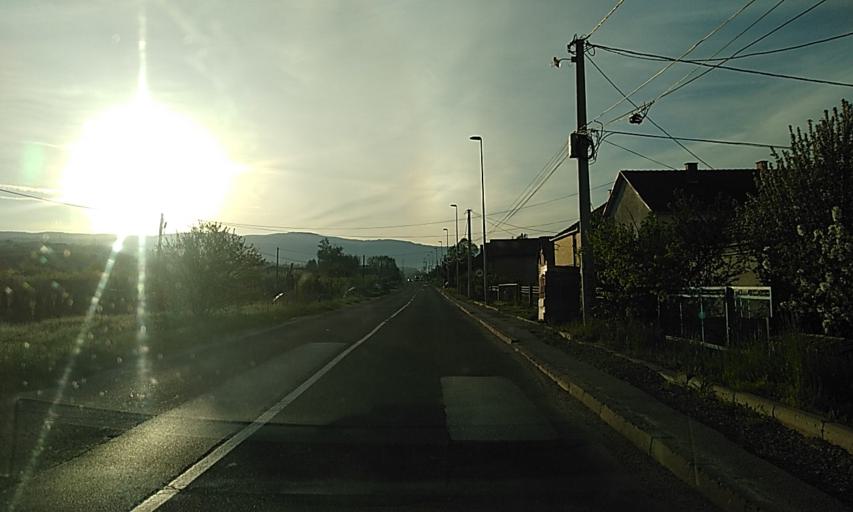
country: RS
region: Central Serbia
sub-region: Pcinjski Okrug
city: Vladicin Han
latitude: 42.7105
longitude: 22.1044
